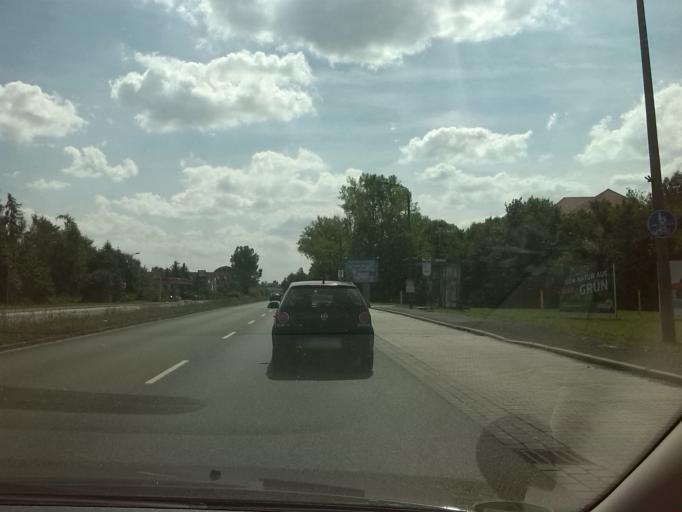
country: DE
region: Saxony
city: Borna
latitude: 51.1357
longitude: 12.5082
